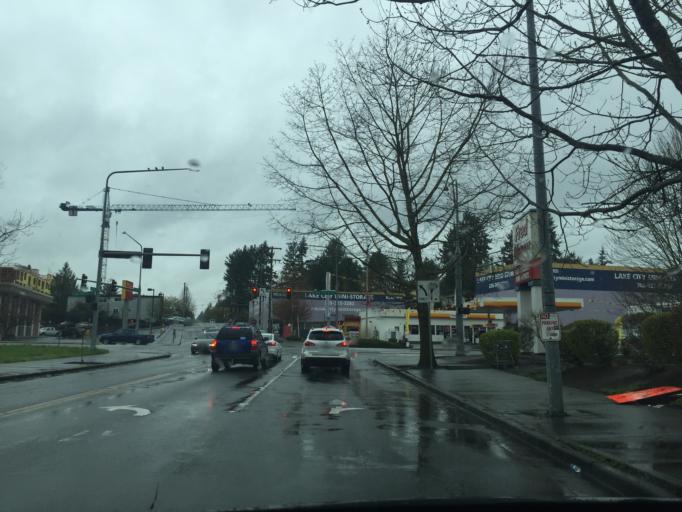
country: US
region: Washington
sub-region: King County
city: Lake Forest Park
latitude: 47.7229
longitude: -122.2925
